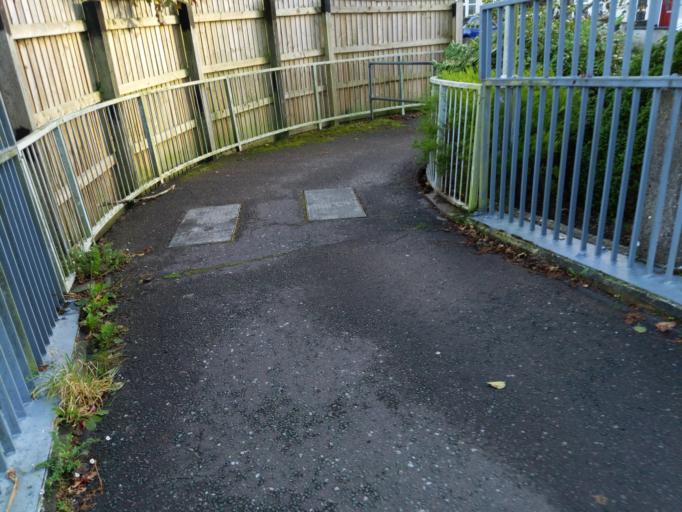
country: GB
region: England
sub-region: Cornwall
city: Torpoint
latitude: 50.4112
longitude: -4.1802
